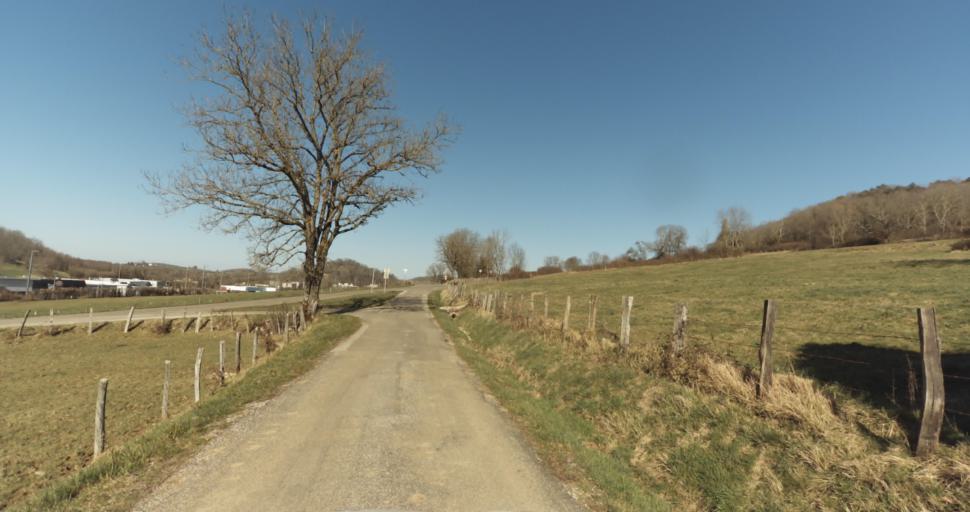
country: FR
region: Franche-Comte
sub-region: Departement du Jura
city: Montmorot
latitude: 46.6669
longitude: 5.5271
